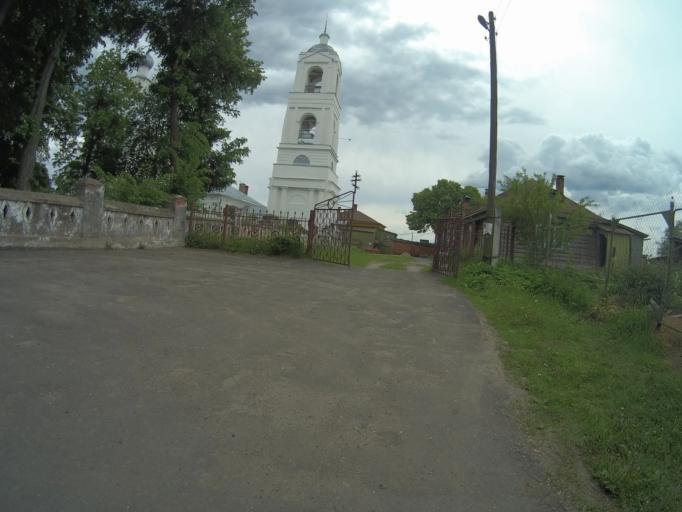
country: RU
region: Vladimir
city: Vorsha
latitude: 56.0477
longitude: 40.1904
